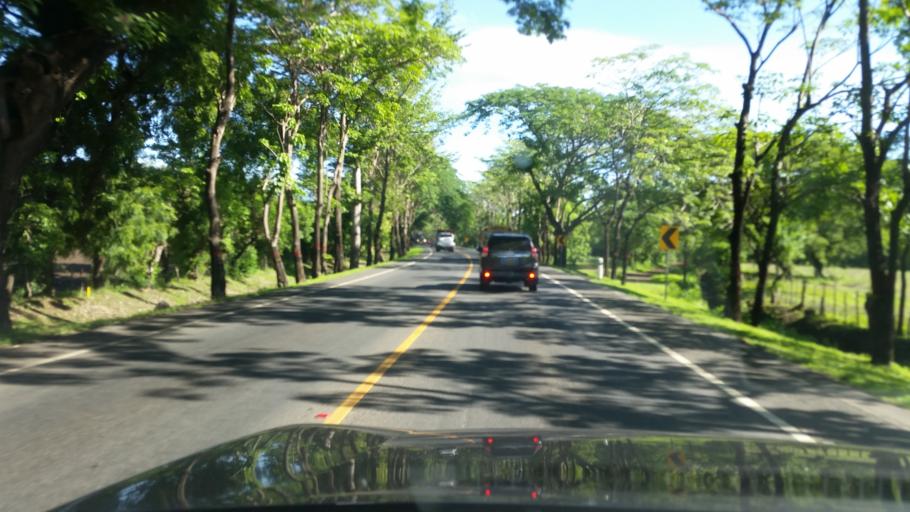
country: NI
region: Leon
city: Telica
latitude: 12.5111
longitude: -86.8606
